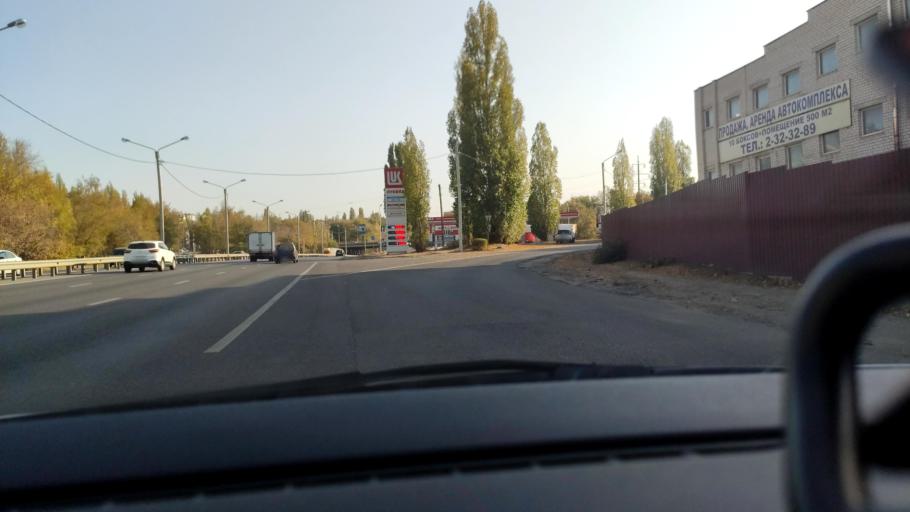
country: RU
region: Voronezj
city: Voronezh
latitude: 51.6577
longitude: 39.1340
